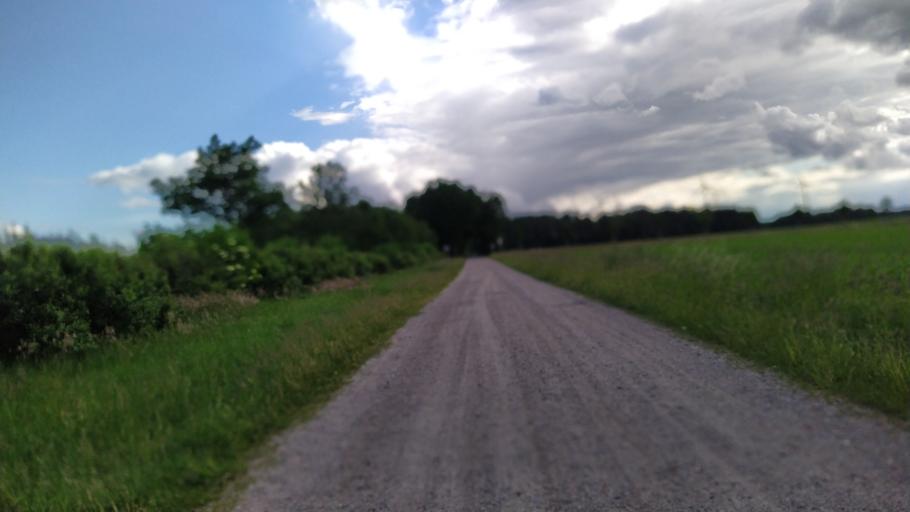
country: DE
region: Lower Saxony
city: Sandbostel
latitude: 53.4321
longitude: 9.1721
